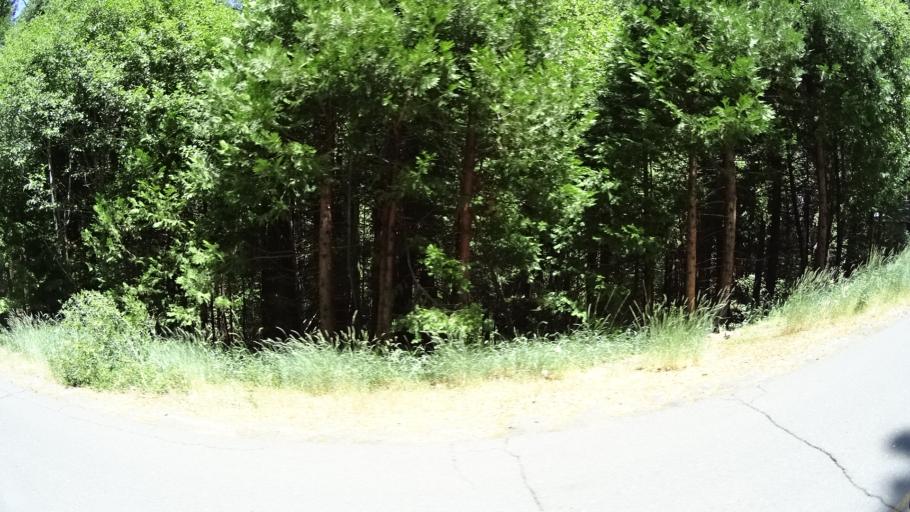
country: US
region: California
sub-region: Calaveras County
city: Arnold
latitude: 38.3136
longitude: -120.2652
